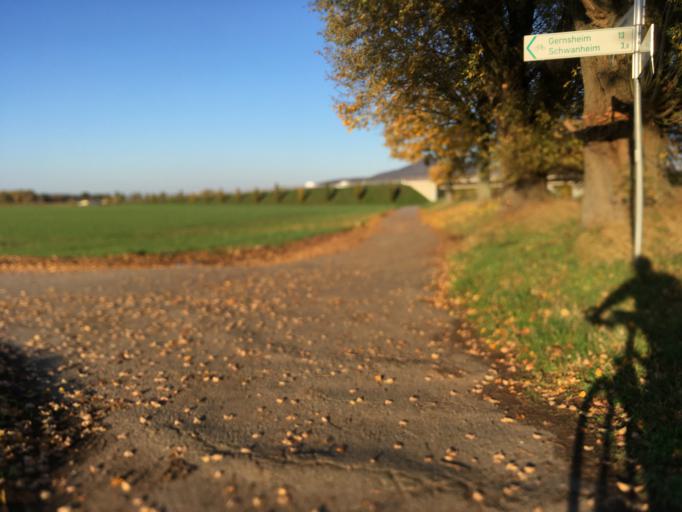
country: DE
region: Hesse
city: Lorsch
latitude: 49.6799
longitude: 8.5838
